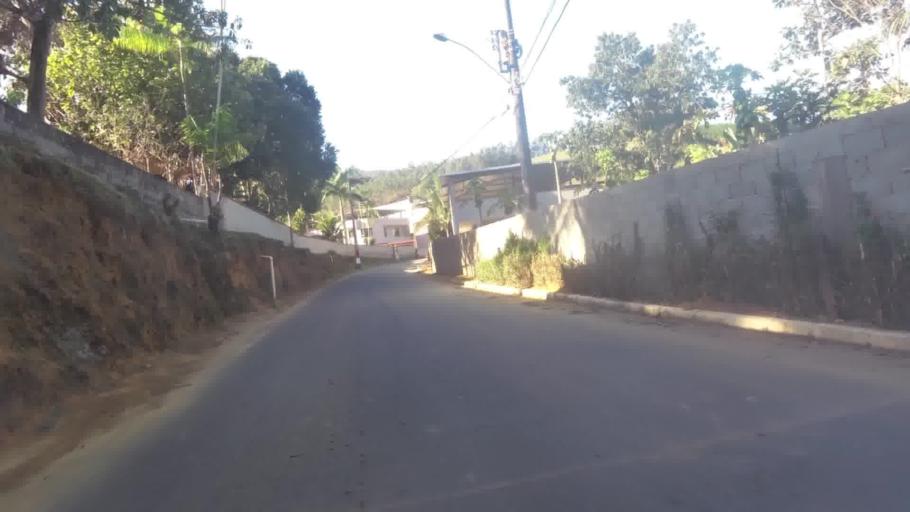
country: BR
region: Espirito Santo
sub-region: Iconha
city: Iconha
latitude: -20.7303
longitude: -40.7791
